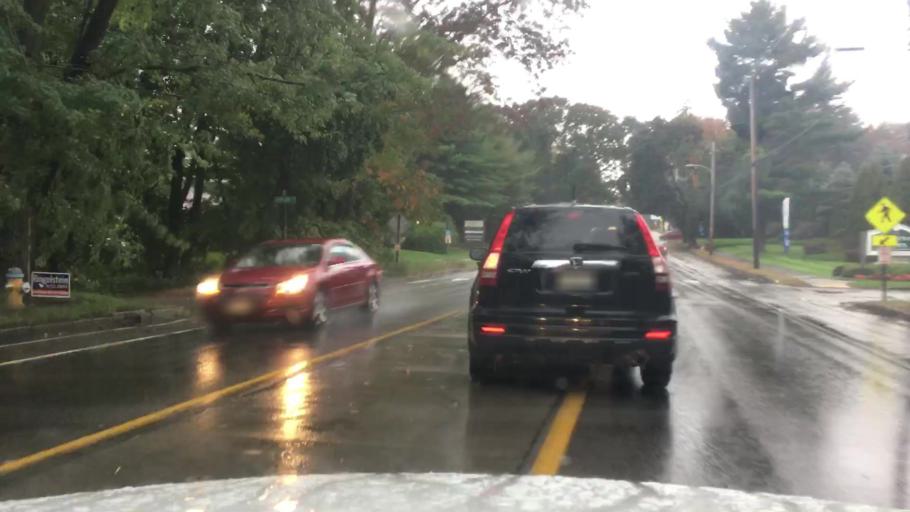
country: US
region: Maine
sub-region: Cumberland County
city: Portland
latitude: 43.6916
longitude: -70.2992
